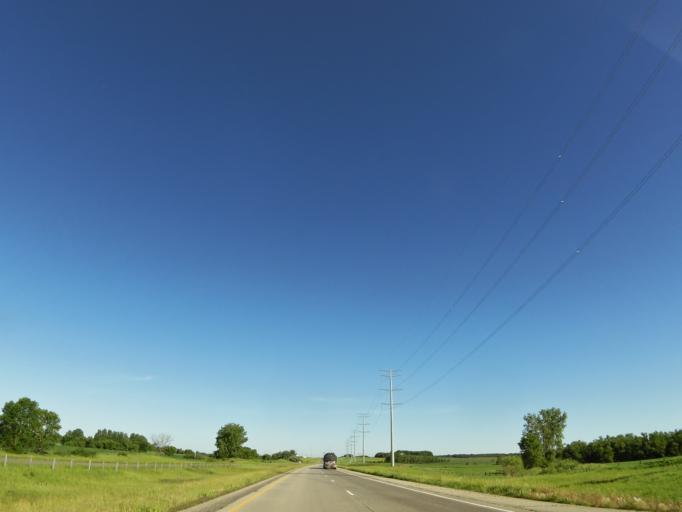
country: US
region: Minnesota
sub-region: Douglas County
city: Alexandria
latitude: 45.9288
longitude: -95.5724
